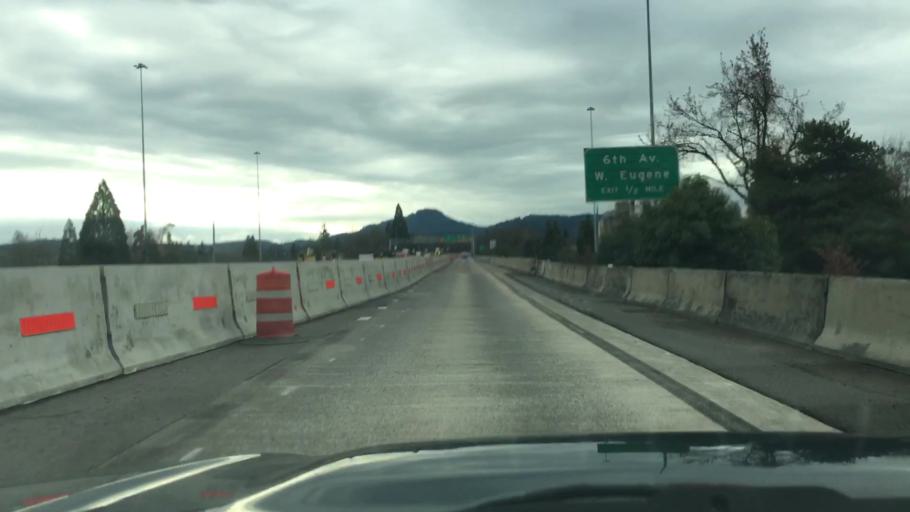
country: US
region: Oregon
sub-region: Lane County
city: Eugene
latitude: 44.0621
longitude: -123.1013
